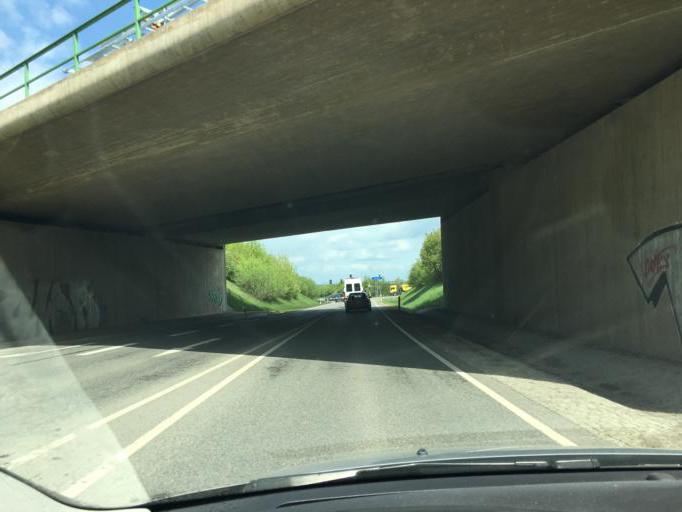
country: DE
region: Saxony
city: Muhlau
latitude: 50.8811
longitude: 12.7822
